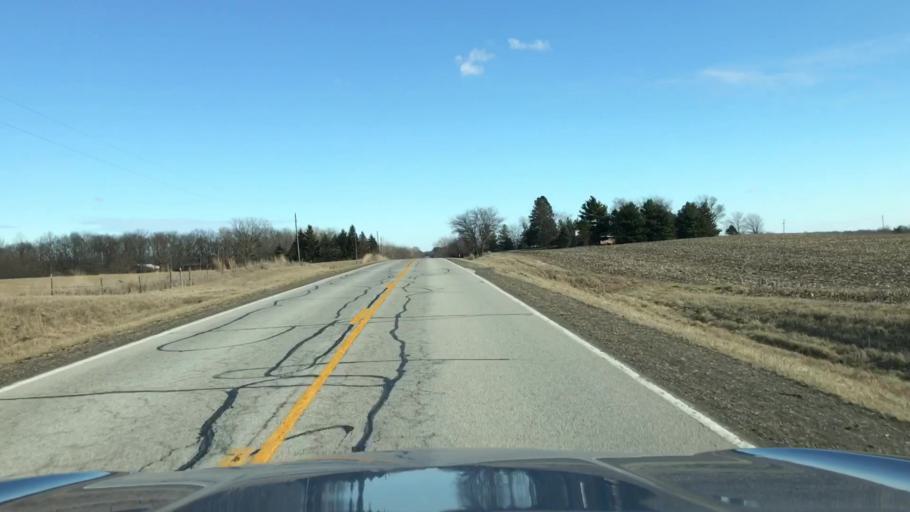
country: US
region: Illinois
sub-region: McLean County
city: Lexington
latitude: 40.6485
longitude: -88.8694
